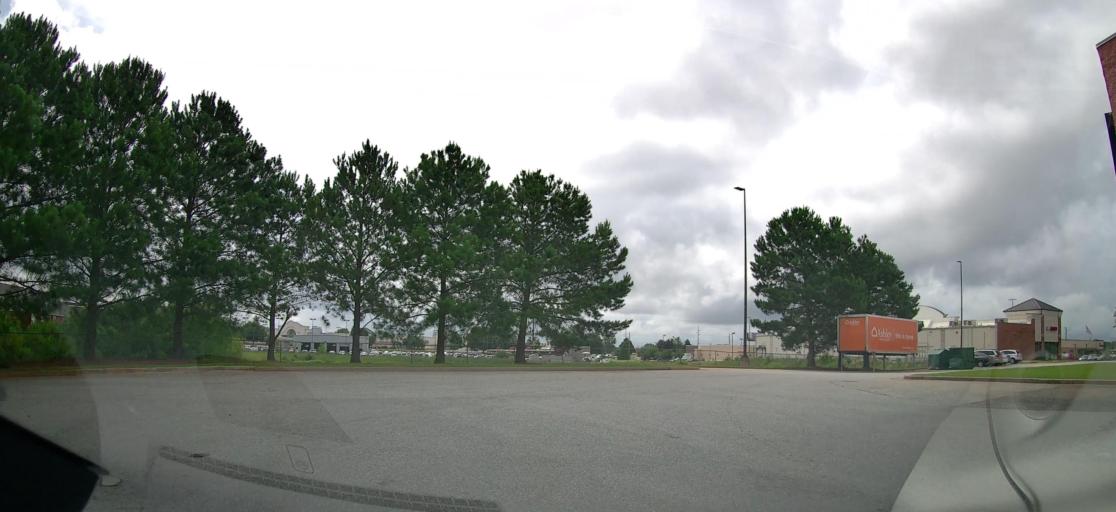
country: US
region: Georgia
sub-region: Houston County
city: Centerville
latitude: 32.6197
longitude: -83.6928
